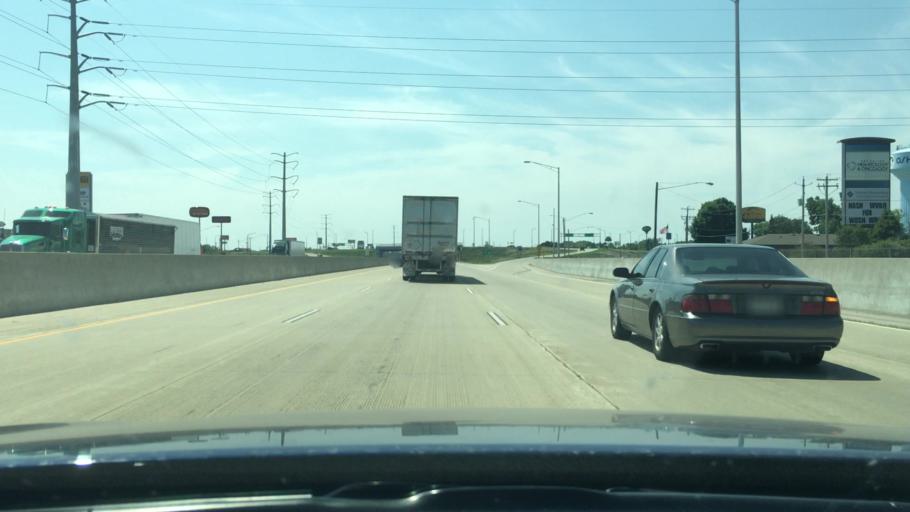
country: US
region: Wisconsin
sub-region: Winnebago County
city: Oshkosh
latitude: 44.0154
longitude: -88.5823
